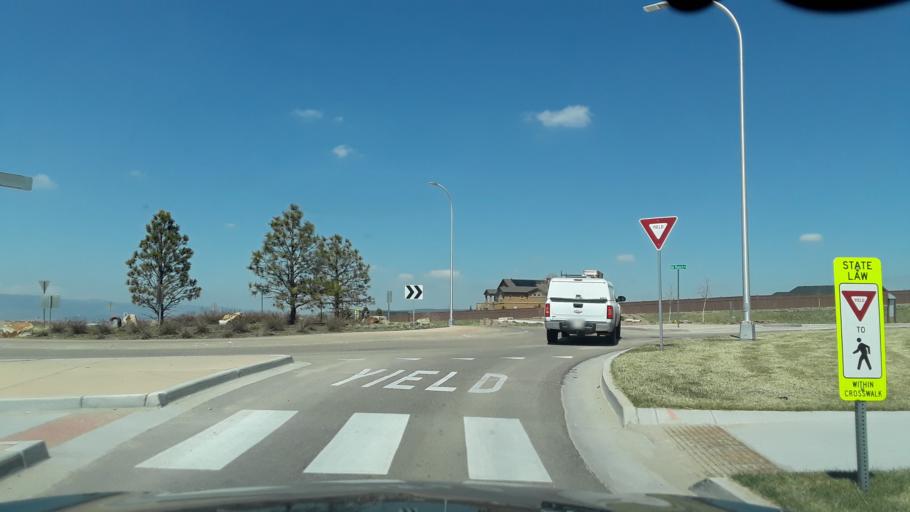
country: US
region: Colorado
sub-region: El Paso County
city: Black Forest
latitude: 38.9832
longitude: -104.7576
